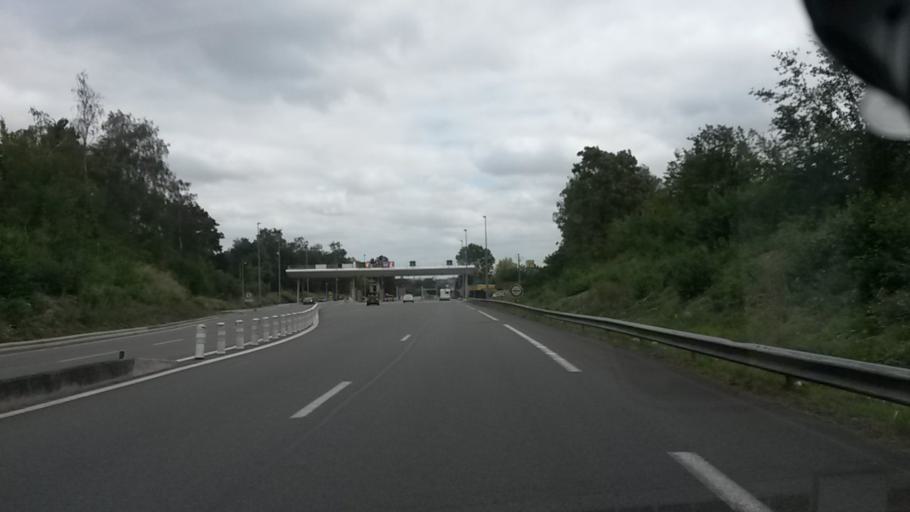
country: FR
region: Nord-Pas-de-Calais
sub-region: Departement du Nord
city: Proville
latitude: 50.1755
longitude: 3.1904
